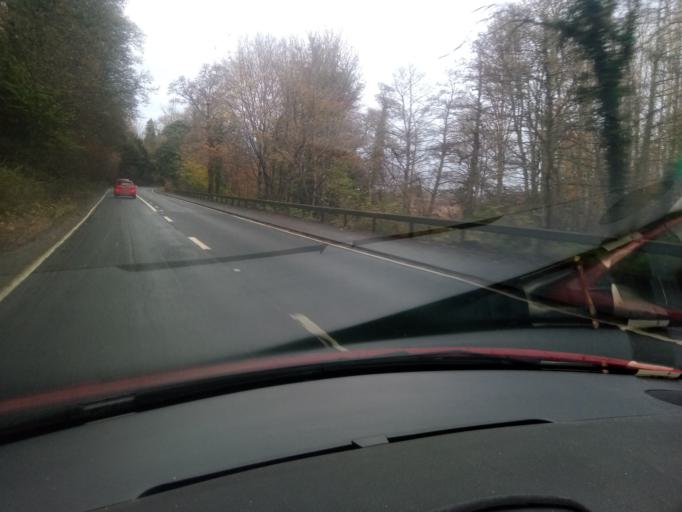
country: GB
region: Scotland
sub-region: The Scottish Borders
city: Jedburgh
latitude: 55.4950
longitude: -2.5458
